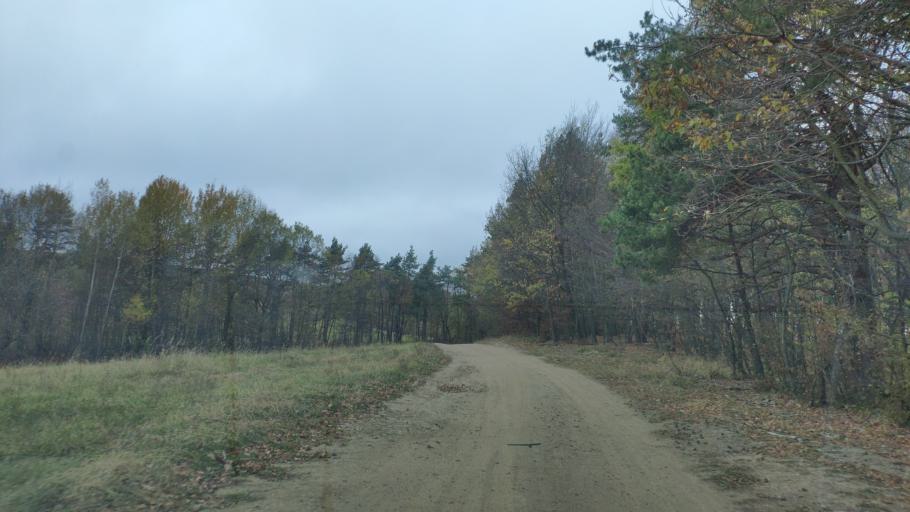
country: SK
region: Presovsky
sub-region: Okres Presov
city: Presov
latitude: 48.9357
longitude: 21.1239
